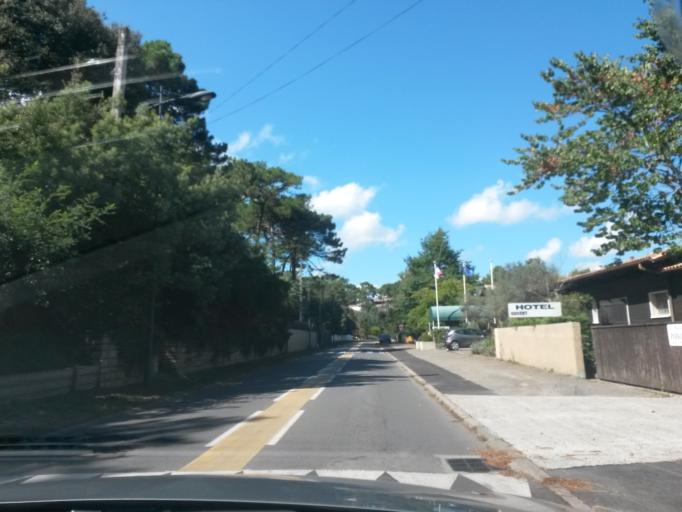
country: FR
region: Aquitaine
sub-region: Departement de la Gironde
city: Arcachon
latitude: 44.6722
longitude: -1.2411
